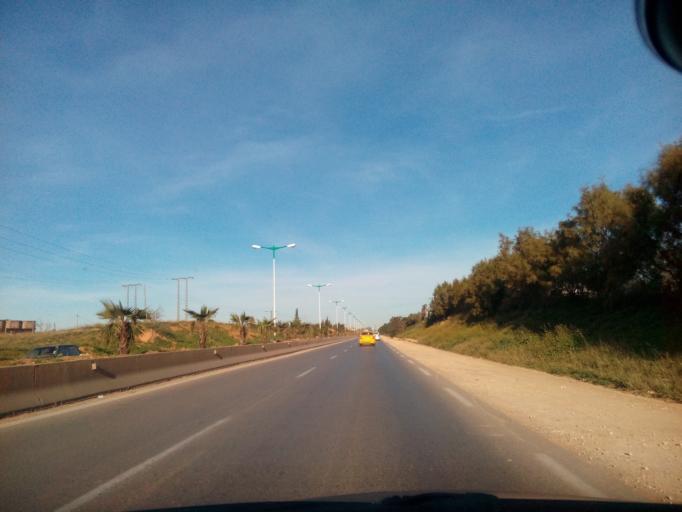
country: DZ
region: Mostaganem
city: Mostaganem
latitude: 35.8631
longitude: 0.1571
